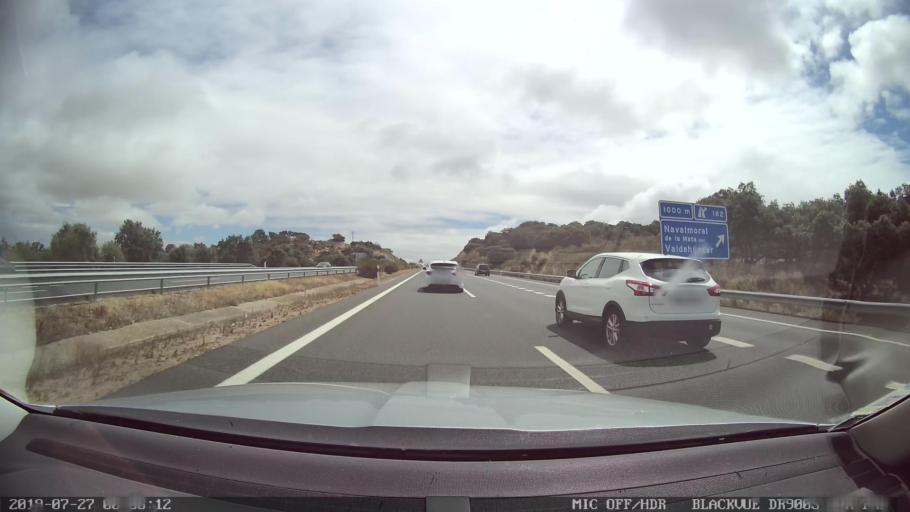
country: ES
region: Extremadura
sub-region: Provincia de Caceres
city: Millanes
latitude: 39.8727
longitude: -5.5642
